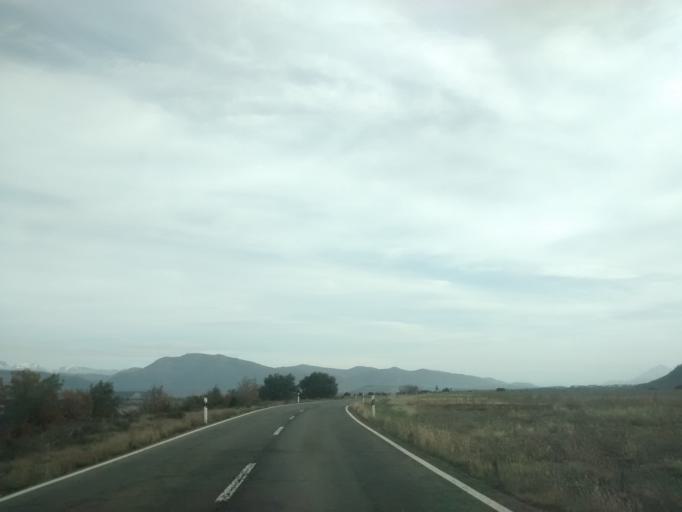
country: ES
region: Aragon
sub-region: Provincia de Zaragoza
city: Mianos
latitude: 42.6107
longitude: -0.8798
